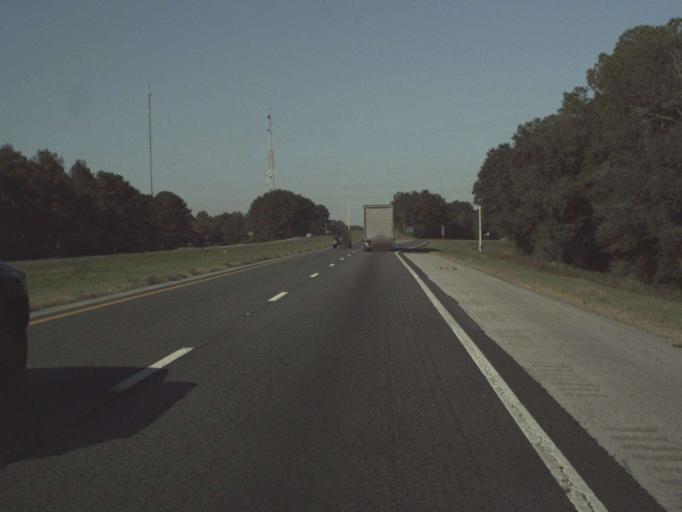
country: US
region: Florida
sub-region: Holmes County
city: Bonifay
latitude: 30.7592
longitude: -85.8066
